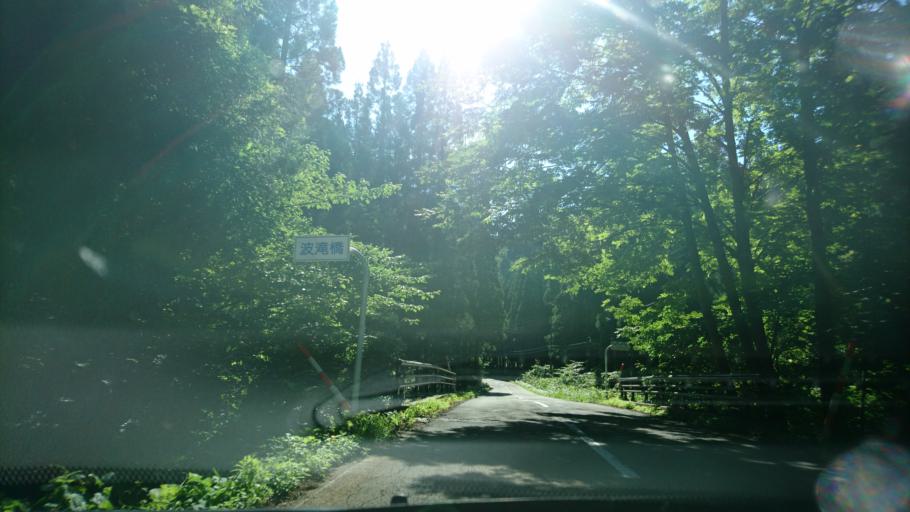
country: JP
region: Akita
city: Kakunodatemachi
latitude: 39.7102
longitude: 140.6124
